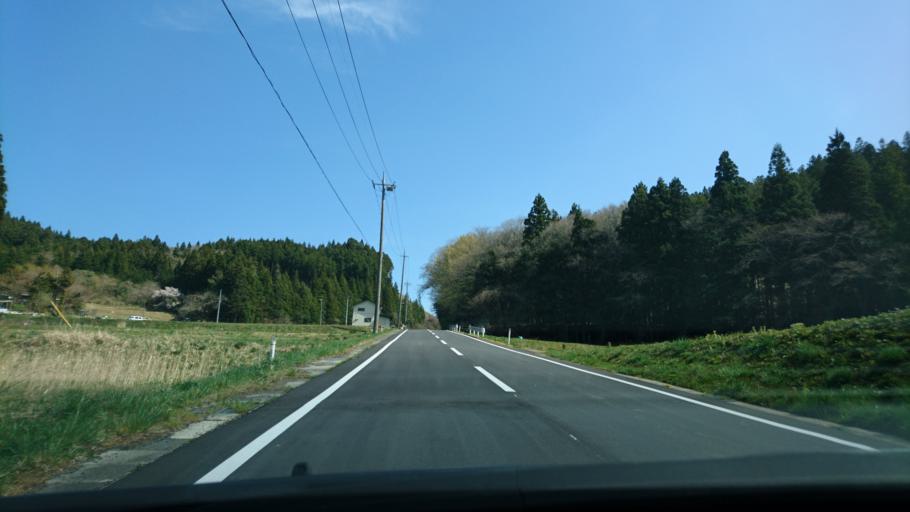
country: JP
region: Iwate
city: Ofunato
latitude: 38.9328
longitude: 141.4506
